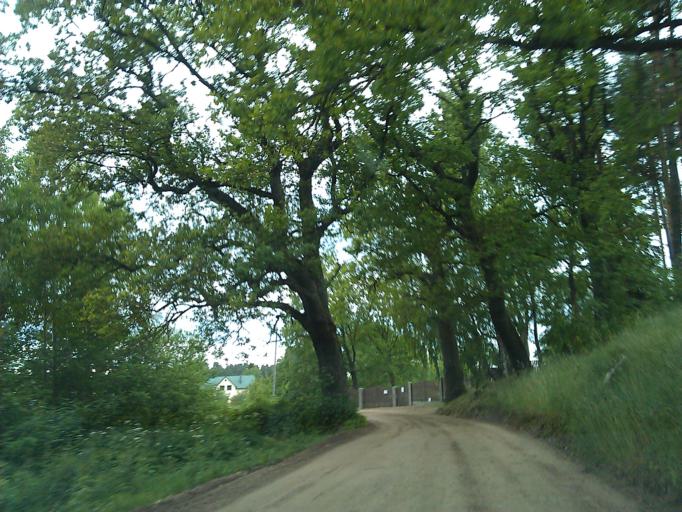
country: LV
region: Adazi
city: Adazi
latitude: 57.0837
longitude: 24.3040
